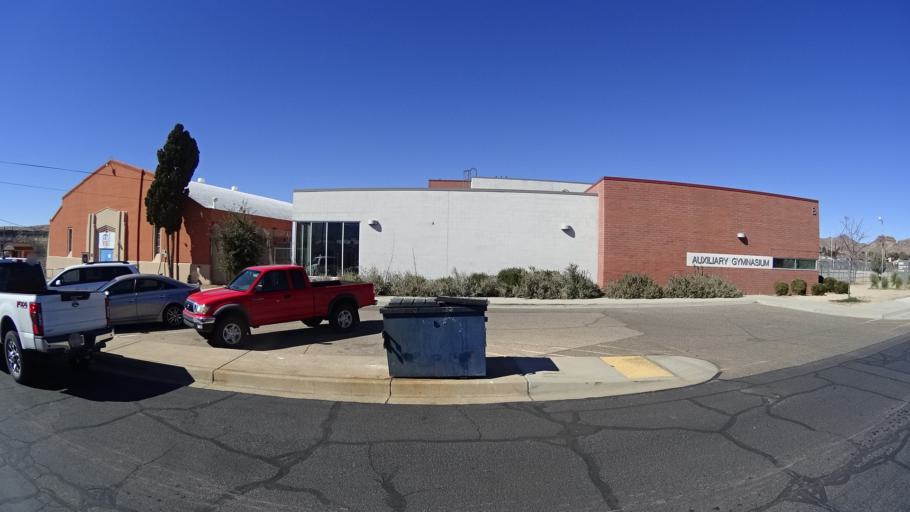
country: US
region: Arizona
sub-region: Mohave County
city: Kingman
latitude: 35.1918
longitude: -114.0578
